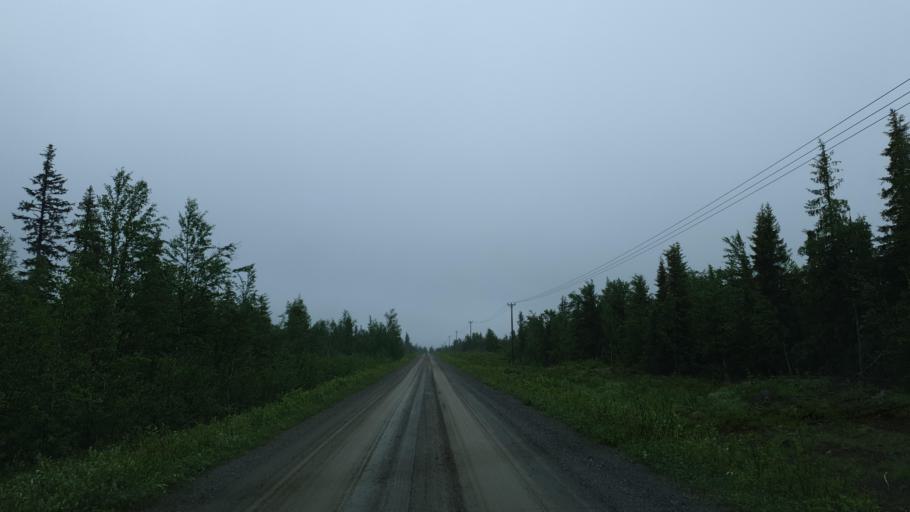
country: SE
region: Vaesterbotten
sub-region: Vilhelmina Kommun
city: Sjoberg
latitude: 65.3143
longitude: 15.9606
